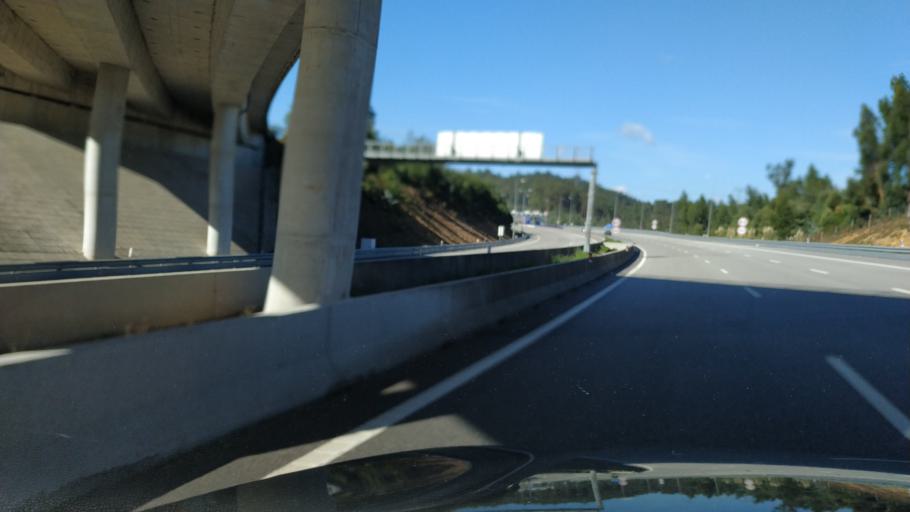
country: PT
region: Porto
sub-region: Vila Nova de Gaia
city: Sandim
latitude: 41.0463
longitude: -8.4994
